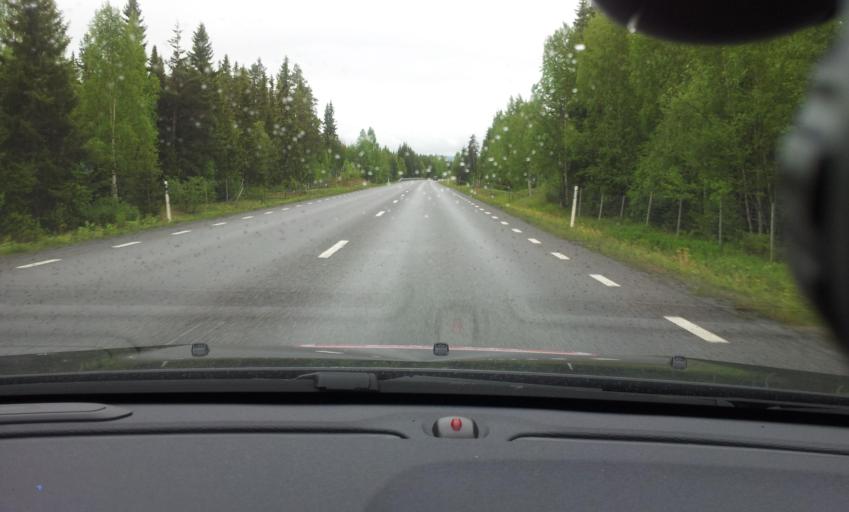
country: SE
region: Jaemtland
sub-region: Krokoms Kommun
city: Valla
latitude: 63.3151
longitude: 13.9316
